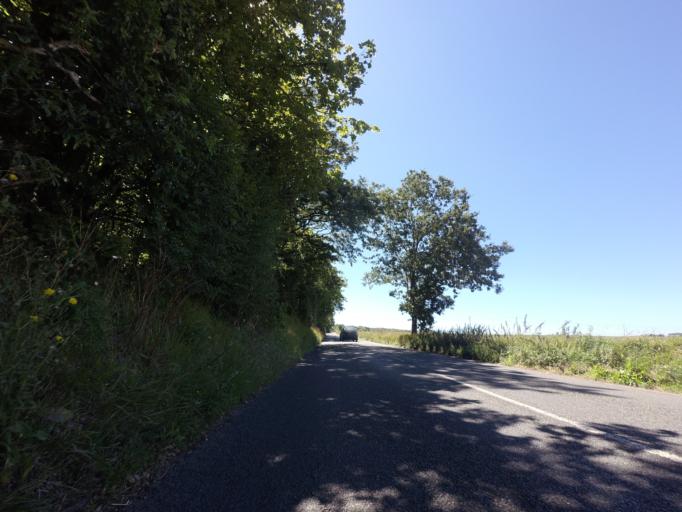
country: GB
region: England
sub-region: Kent
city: Eastry
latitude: 51.2374
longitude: 1.3074
